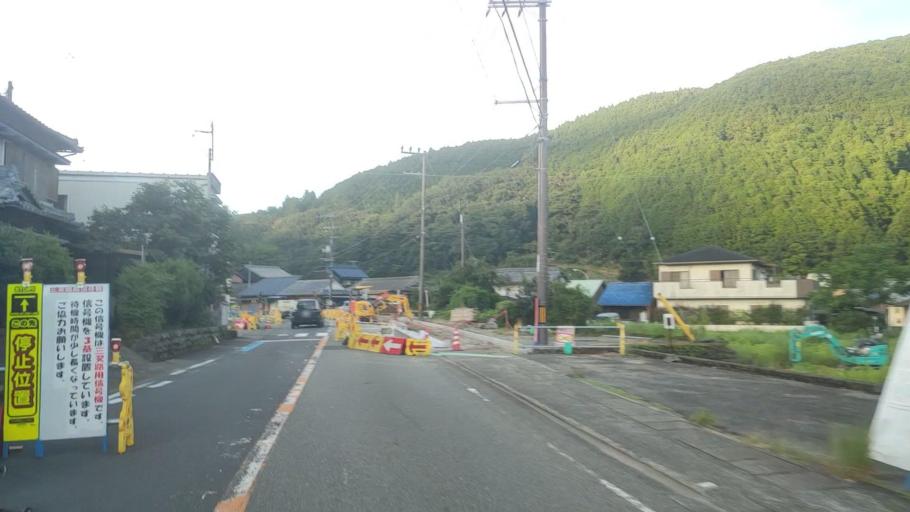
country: JP
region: Wakayama
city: Tanabe
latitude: 33.7933
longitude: 135.5181
